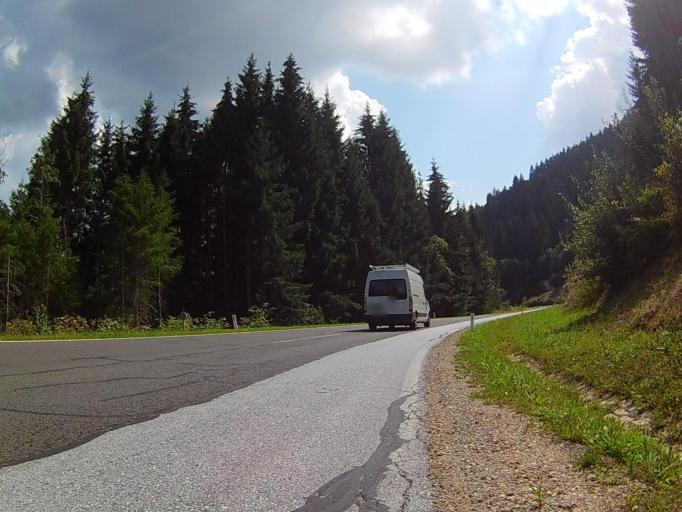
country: AT
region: Styria
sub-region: Politischer Bezirk Deutschlandsberg
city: Soboth
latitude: 46.7022
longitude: 15.0961
